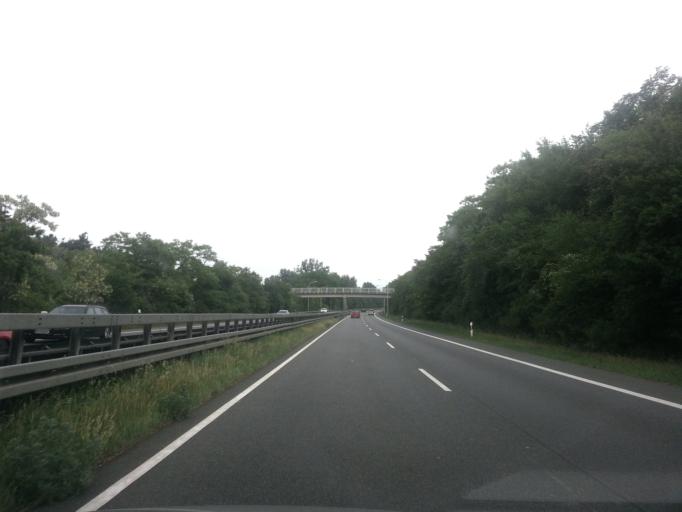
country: DE
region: Hesse
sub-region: Regierungsbezirk Darmstadt
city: Darmstadt
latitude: 49.8449
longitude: 8.6392
